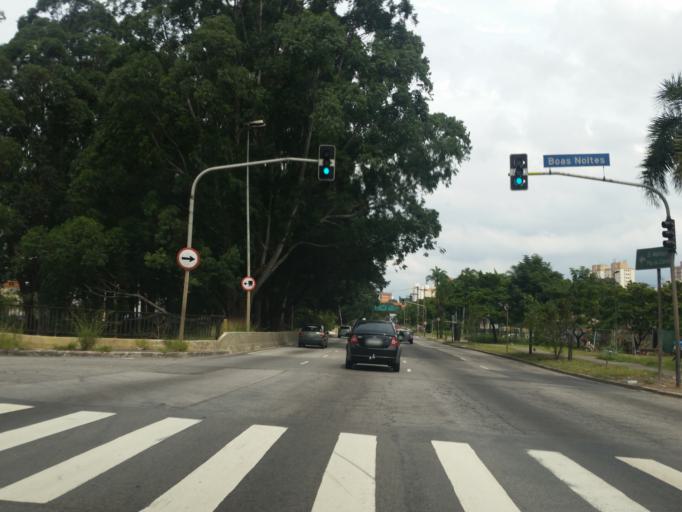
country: BR
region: Sao Paulo
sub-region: Ferraz De Vasconcelos
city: Ferraz de Vasconcelos
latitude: -23.5277
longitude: -46.4578
